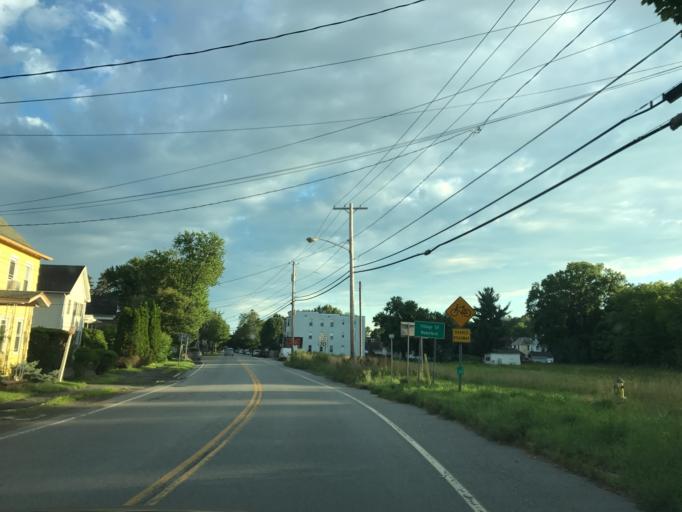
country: US
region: New York
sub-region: Saratoga County
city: Waterford
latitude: 42.7964
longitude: -73.6742
